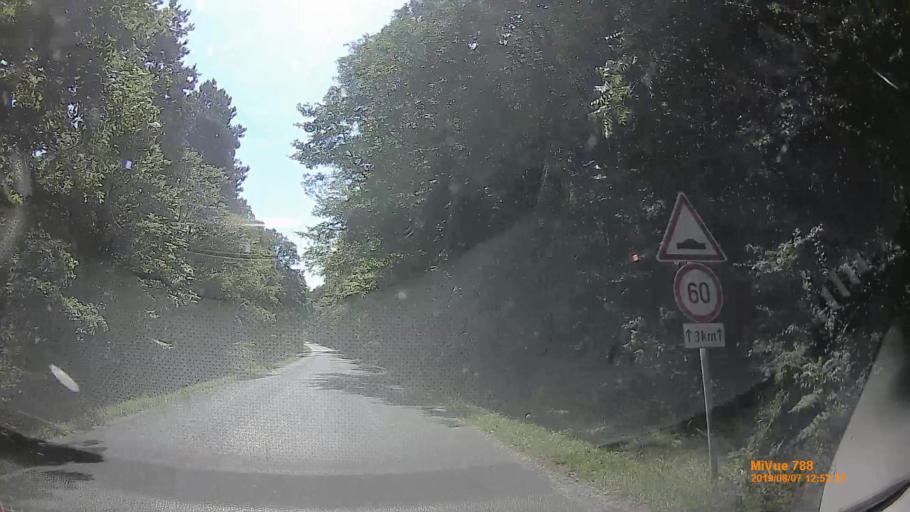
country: HU
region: Zala
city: Cserszegtomaj
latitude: 46.8491
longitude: 17.2674
